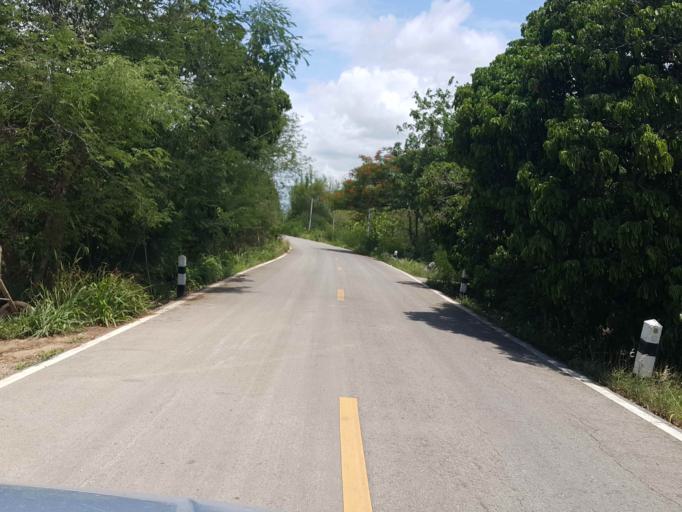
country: TH
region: Lamphun
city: Pa Sang
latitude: 18.5167
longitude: 98.8743
